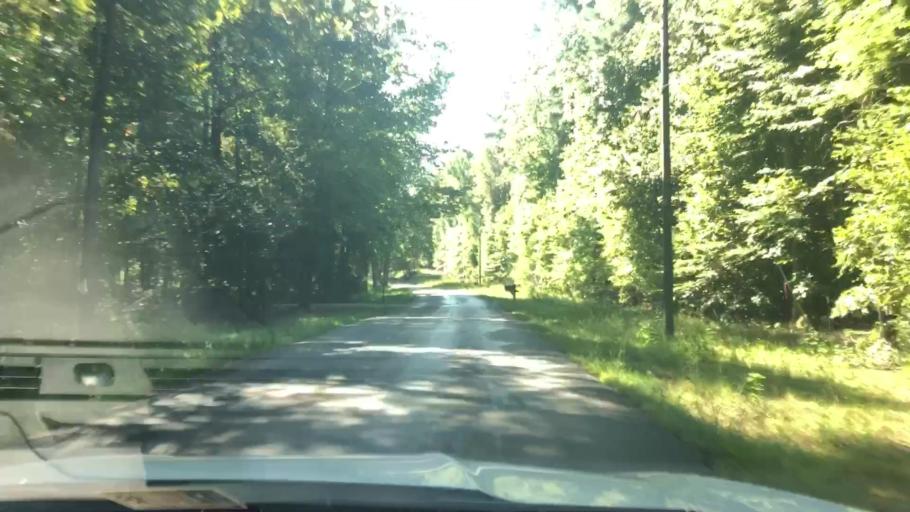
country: US
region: Virginia
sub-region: New Kent County
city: New Kent
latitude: 37.4759
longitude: -76.9330
